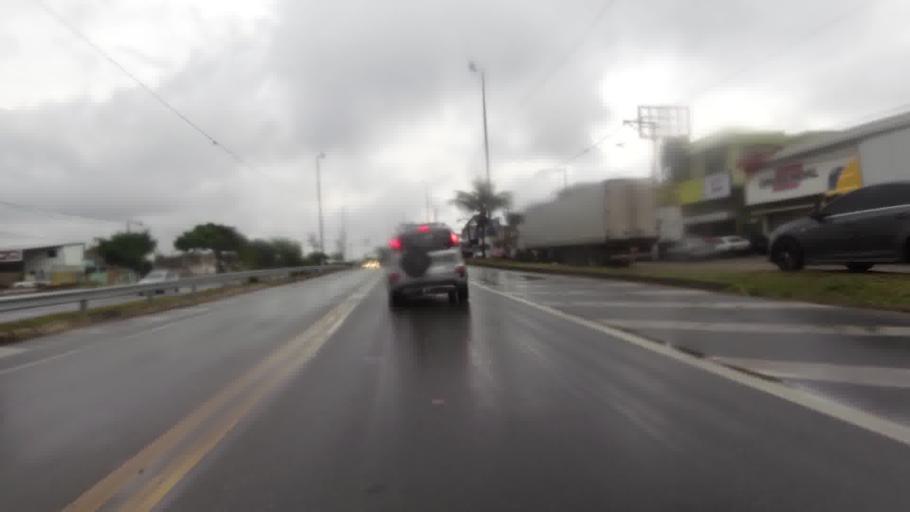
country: BR
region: Rio de Janeiro
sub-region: Campos Dos Goytacazes
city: Campos
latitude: -21.7237
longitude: -41.3190
